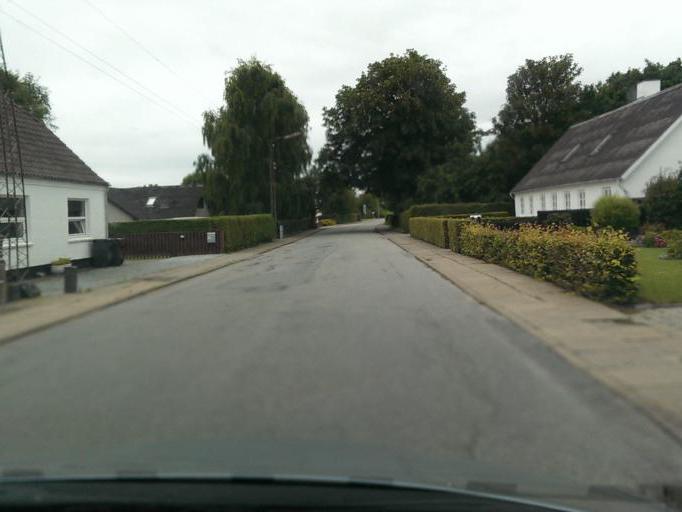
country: DK
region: North Denmark
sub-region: Hjorring Kommune
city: Vra
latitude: 57.3523
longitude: 9.9337
